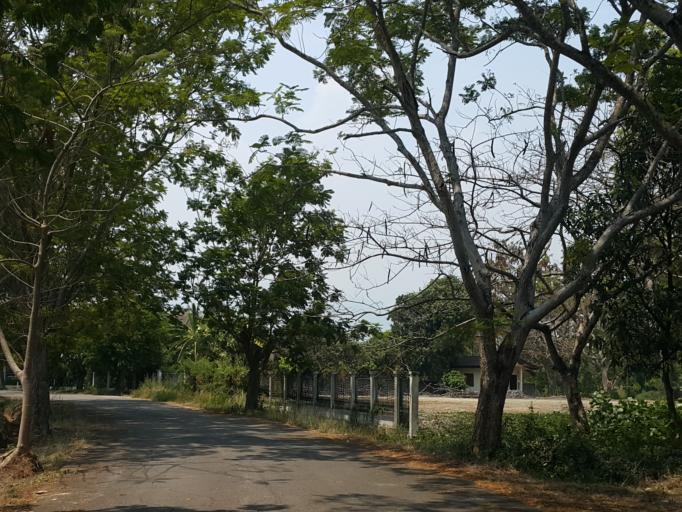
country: TH
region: Chiang Mai
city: Chiang Mai
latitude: 18.7312
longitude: 98.9762
